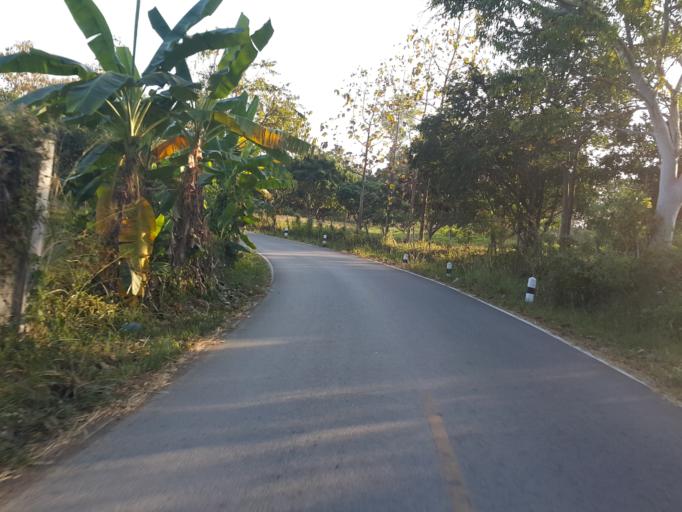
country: TH
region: Chiang Mai
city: Mae On
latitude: 18.7983
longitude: 99.2502
